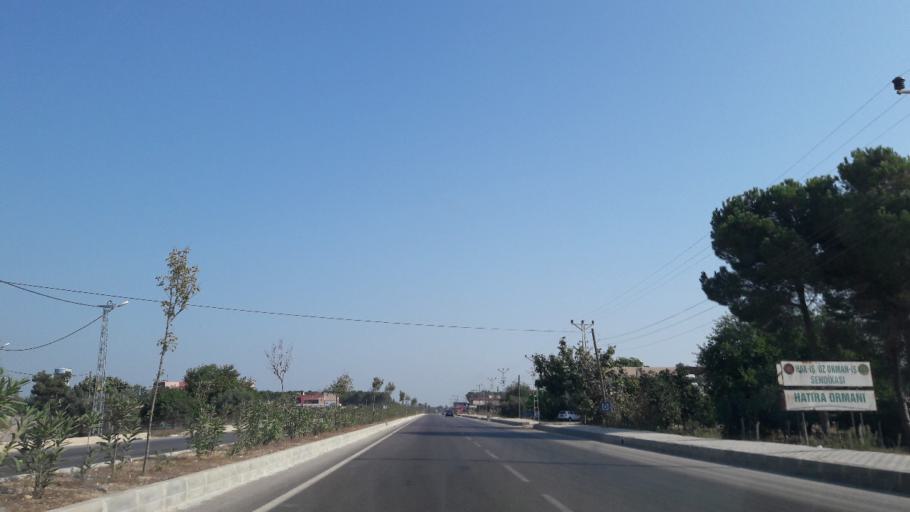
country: TR
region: Adana
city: Yakapinar
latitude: 37.1140
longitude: 35.5126
